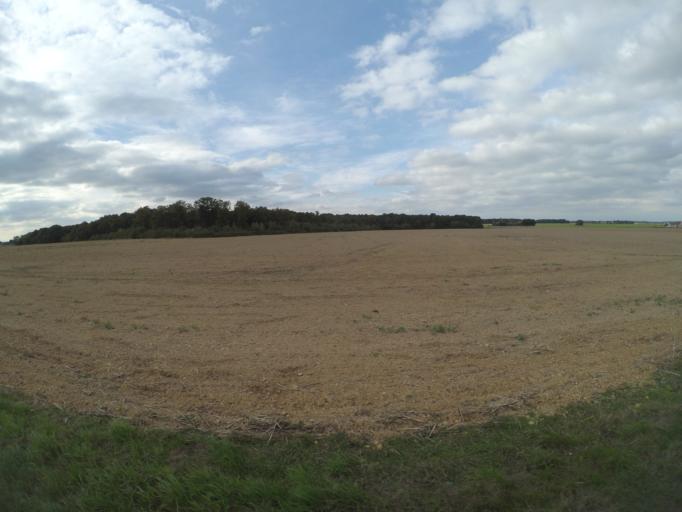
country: FR
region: Centre
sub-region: Departement d'Indre-et-Loire
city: Nazelles-Negron
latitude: 47.4650
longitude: 0.9380
